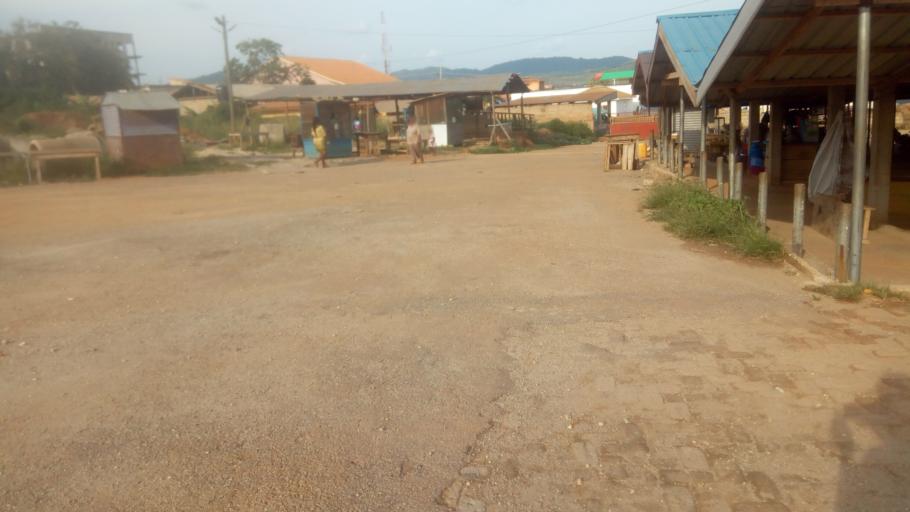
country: GH
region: Ashanti
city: Obuasi
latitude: 6.2137
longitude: -1.6900
